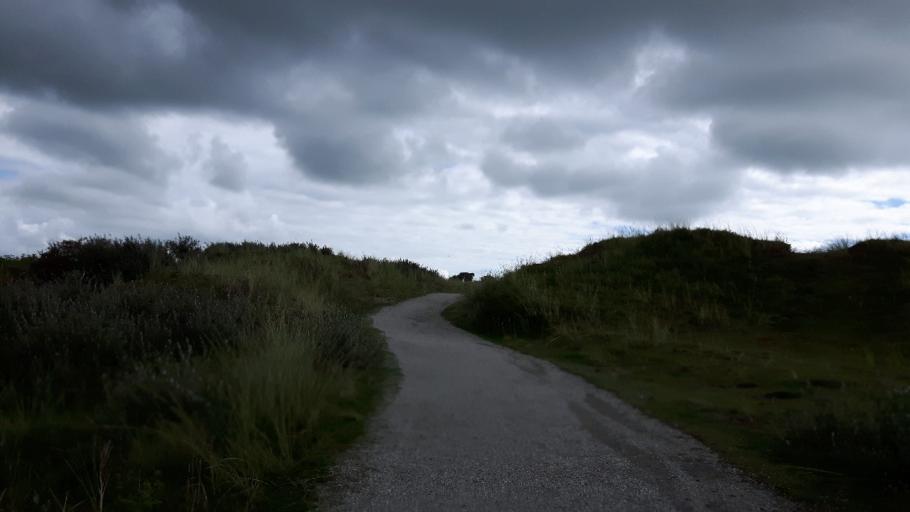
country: NL
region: Friesland
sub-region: Gemeente Ameland
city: Hollum
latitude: 53.4524
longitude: 5.6200
